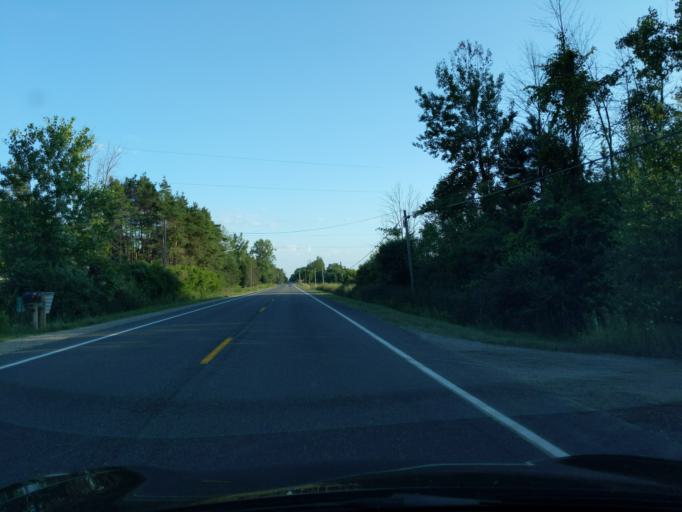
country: US
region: Michigan
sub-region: Midland County
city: Midland
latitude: 43.5722
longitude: -84.3695
